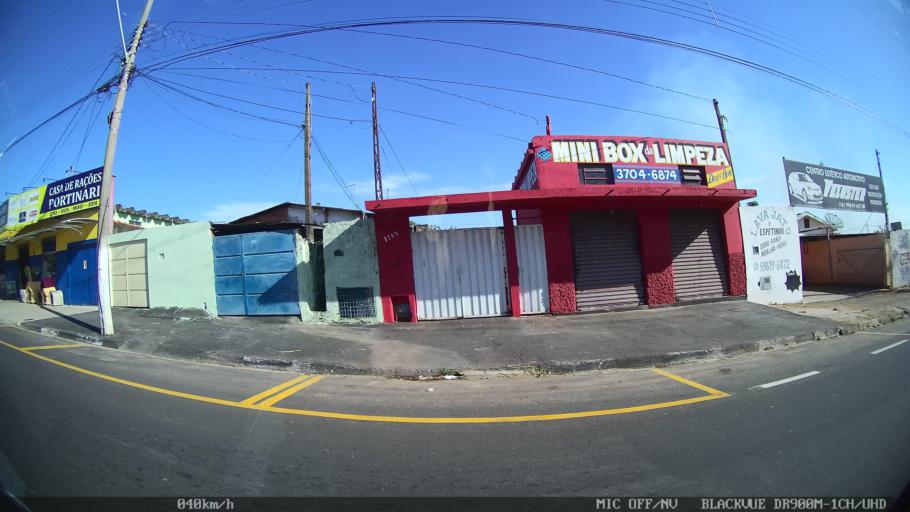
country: BR
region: Sao Paulo
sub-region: Franca
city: Franca
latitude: -20.4960
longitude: -47.4229
